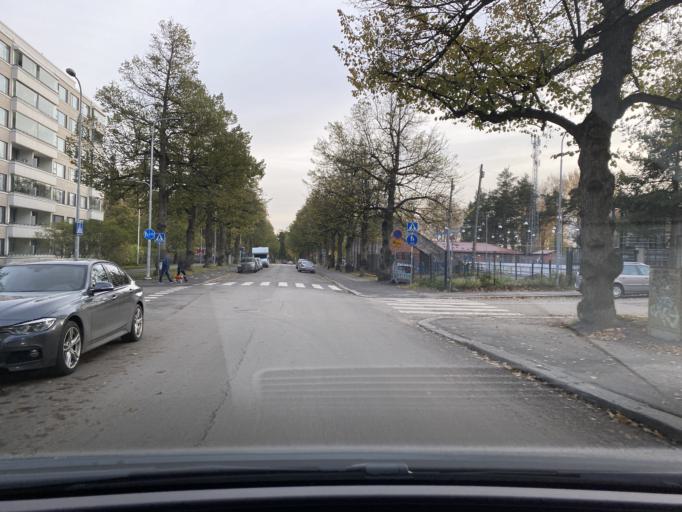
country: FI
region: Pirkanmaa
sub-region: Tampere
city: Tampere
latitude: 61.4932
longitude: 23.7482
